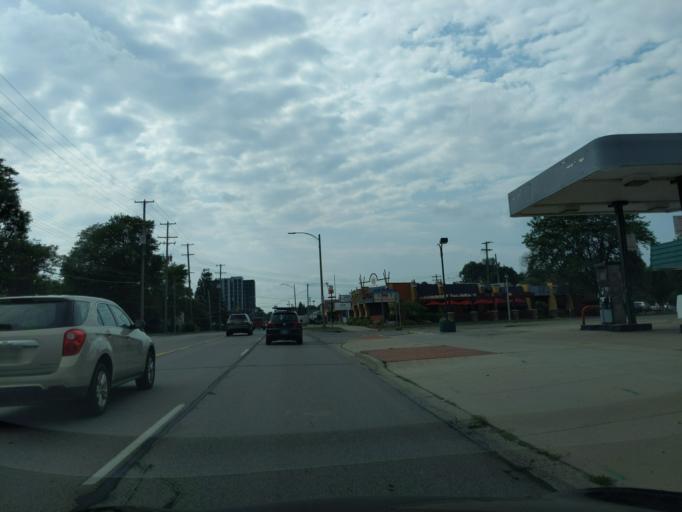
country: US
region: Michigan
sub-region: Ingham County
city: East Lansing
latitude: 42.7303
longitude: -84.4654
